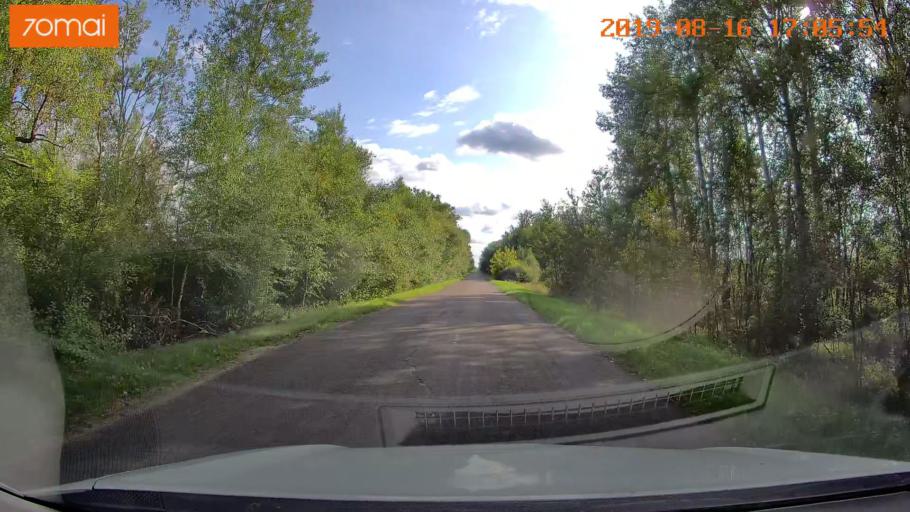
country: BY
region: Mogilev
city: Hlusha
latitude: 53.2328
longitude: 28.9392
